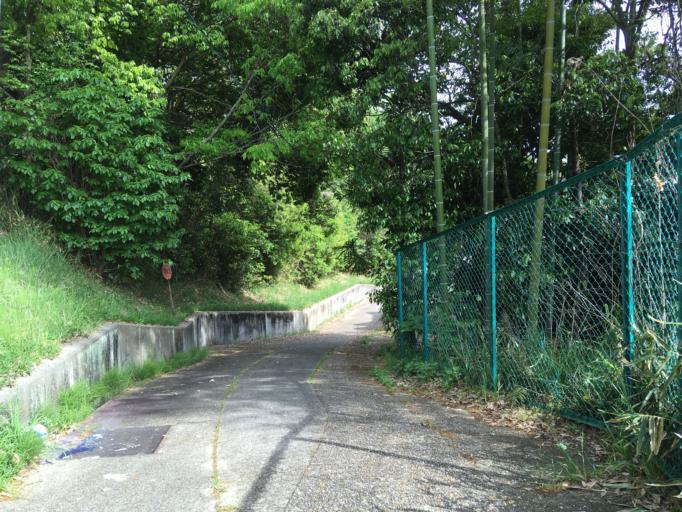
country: JP
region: Nara
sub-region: Ikoma-shi
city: Ikoma
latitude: 34.7065
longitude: 135.7100
